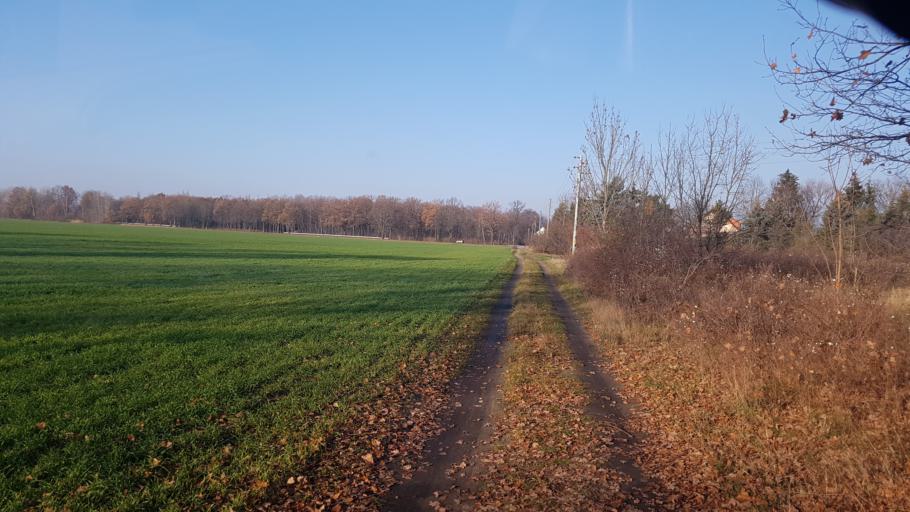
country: DE
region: Brandenburg
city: Lauchhammer
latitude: 51.4608
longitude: 13.7505
